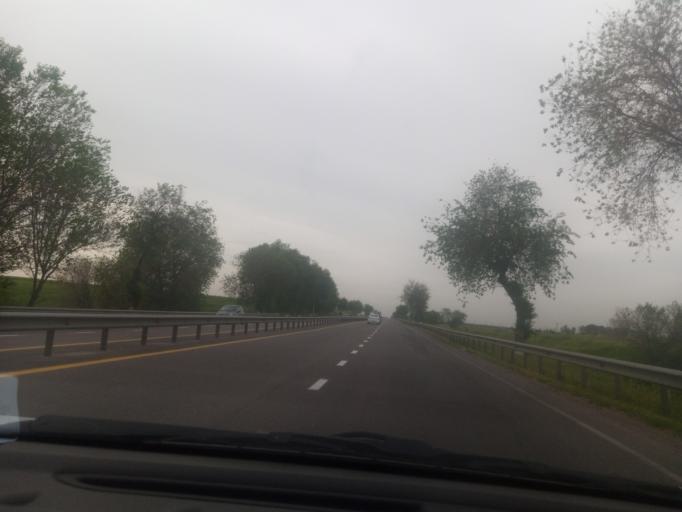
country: UZ
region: Toshkent
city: Tuytepa
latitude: 41.1052
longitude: 69.4526
